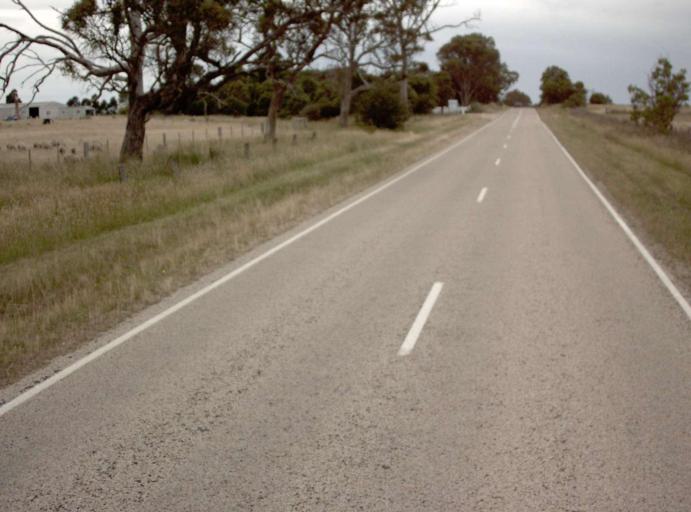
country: AU
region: Victoria
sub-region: East Gippsland
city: Bairnsdale
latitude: -37.9087
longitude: 147.5512
